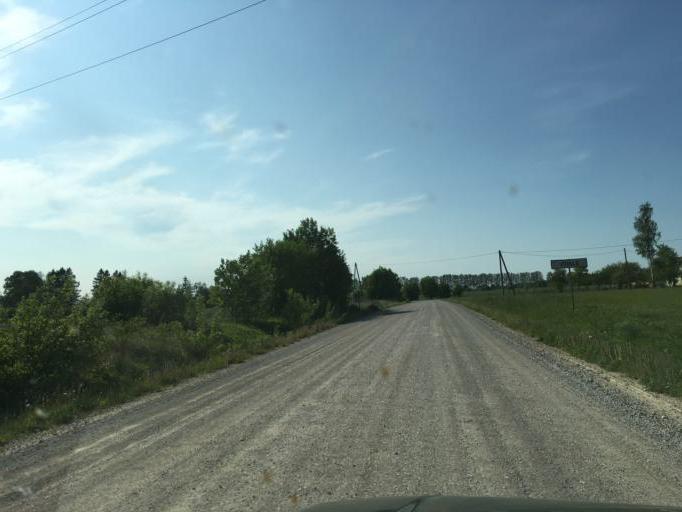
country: LV
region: Dundaga
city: Dundaga
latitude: 57.6077
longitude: 22.4612
